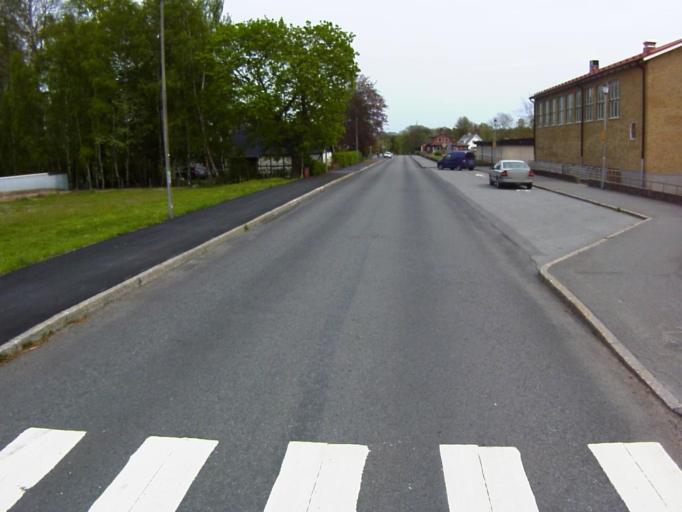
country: SE
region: Skane
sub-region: Kristianstads Kommun
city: Onnestad
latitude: 55.9318
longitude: 13.9656
